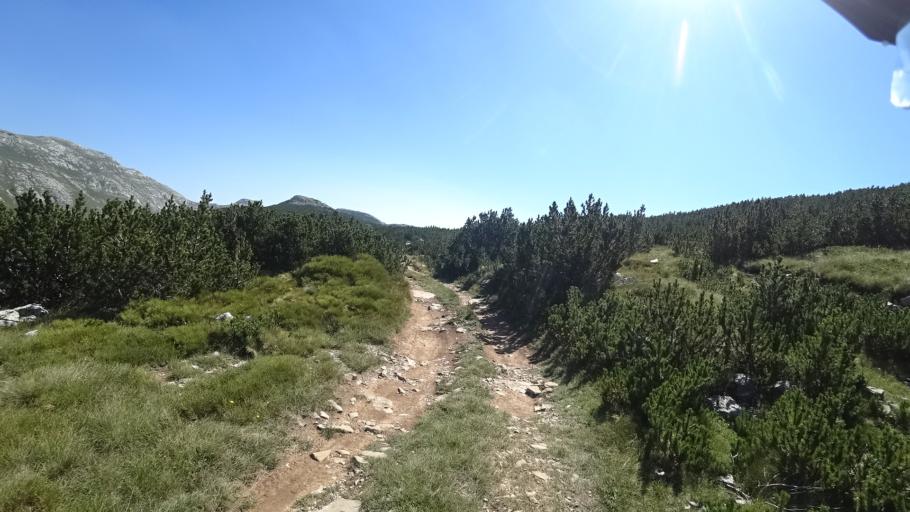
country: HR
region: Splitsko-Dalmatinska
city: Hrvace
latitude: 43.9360
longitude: 16.5727
